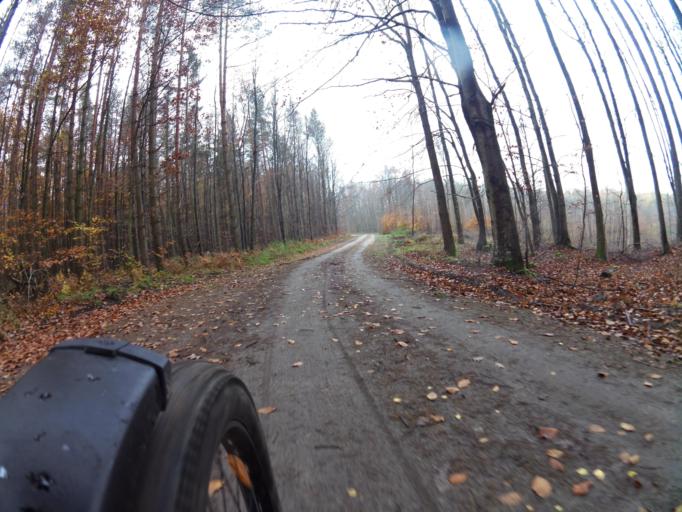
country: PL
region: Pomeranian Voivodeship
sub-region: Powiat pucki
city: Krokowa
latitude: 54.7720
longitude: 18.0931
